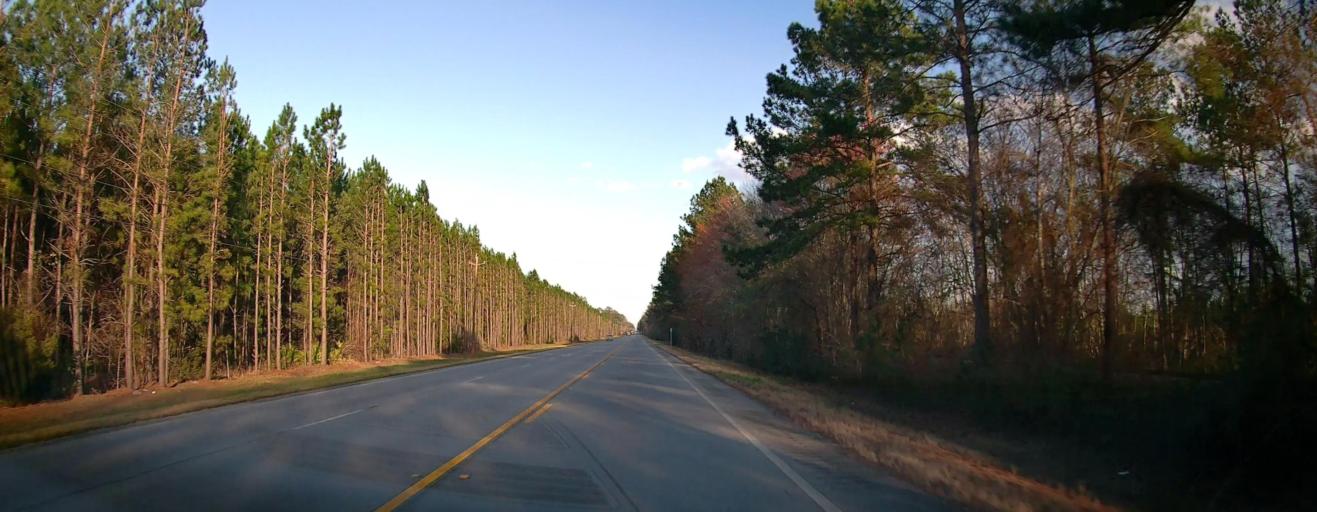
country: US
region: Georgia
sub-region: Bryan County
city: Pembroke
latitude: 32.1434
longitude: -81.7318
